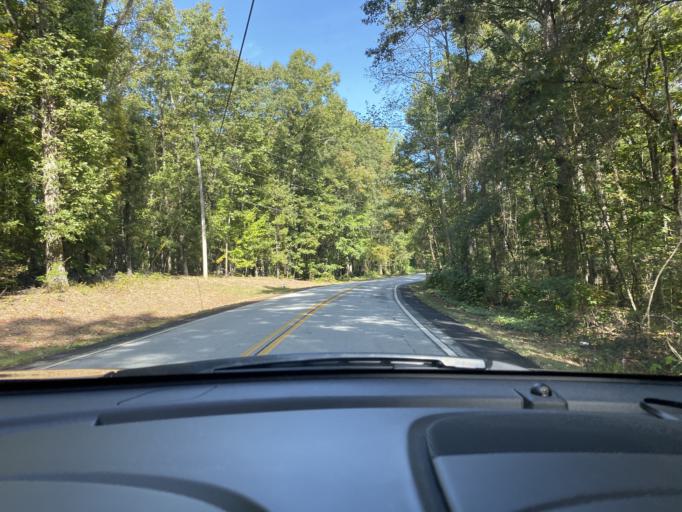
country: US
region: Georgia
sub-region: Gwinnett County
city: Grayson
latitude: 33.8886
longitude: -83.9079
